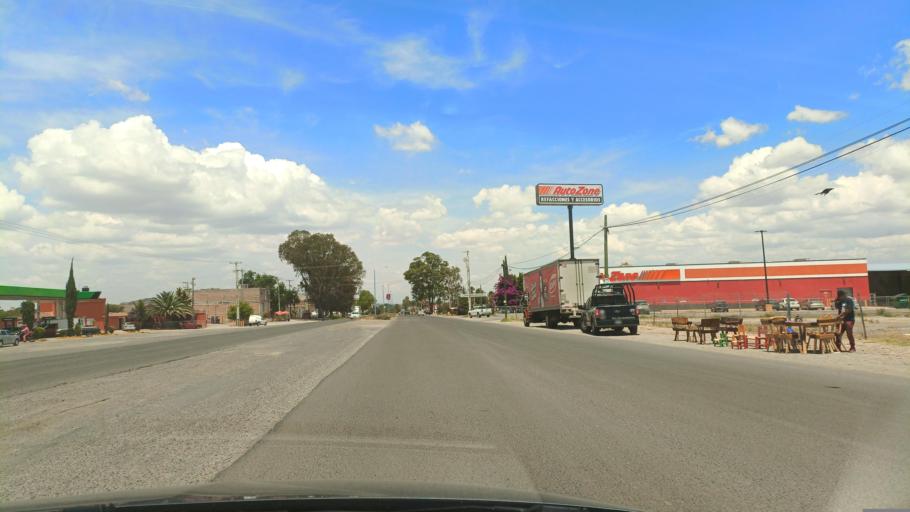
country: MX
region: Guanajuato
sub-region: San Luis de la Paz
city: San Ignacio
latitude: 21.2935
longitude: -100.5371
